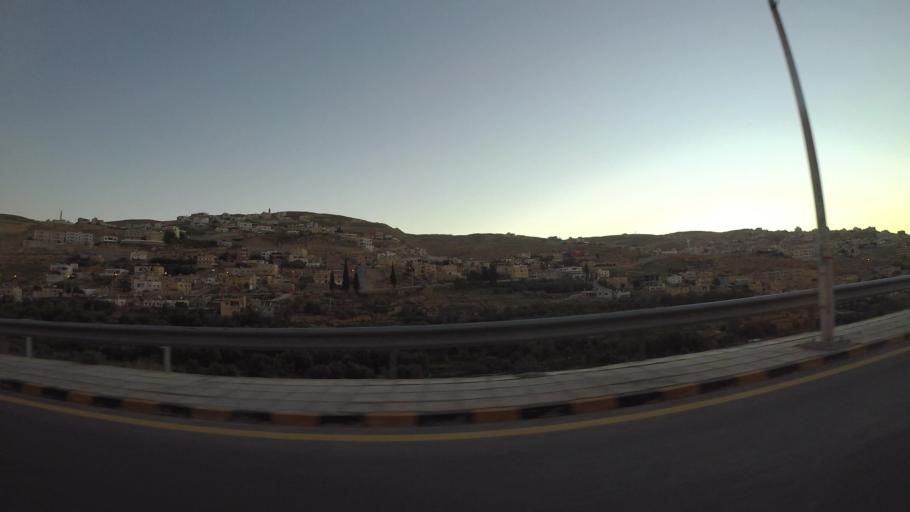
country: JO
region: Ma'an
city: Petra
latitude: 30.3138
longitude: 35.4836
